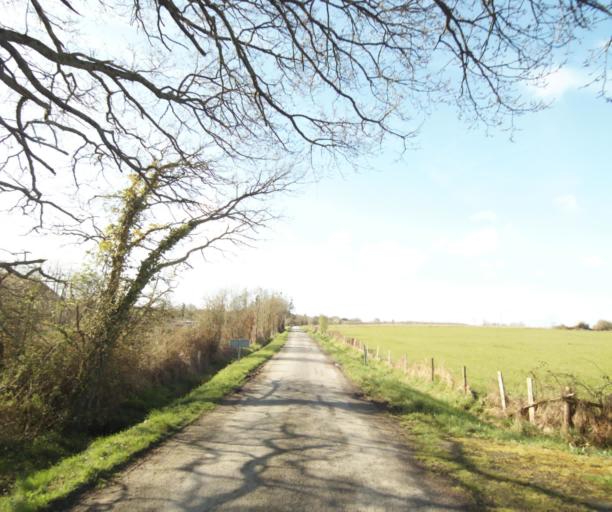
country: FR
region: Pays de la Loire
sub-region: Departement de la Loire-Atlantique
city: Bouvron
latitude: 47.4120
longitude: -1.8467
